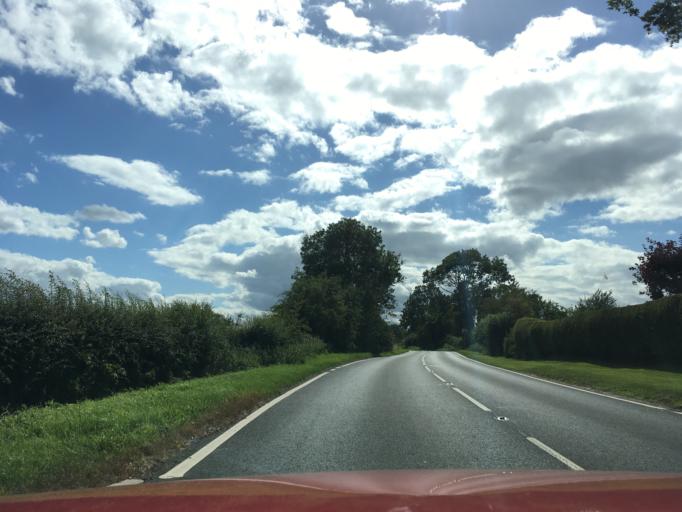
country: GB
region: England
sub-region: Leicestershire
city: Shepshed
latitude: 52.7805
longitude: -1.3355
